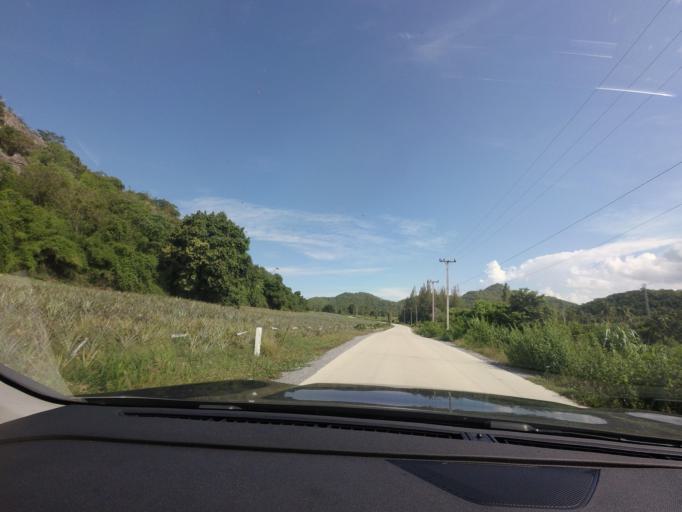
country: TH
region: Prachuap Khiri Khan
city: Hua Hin
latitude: 12.4758
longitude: 99.9368
